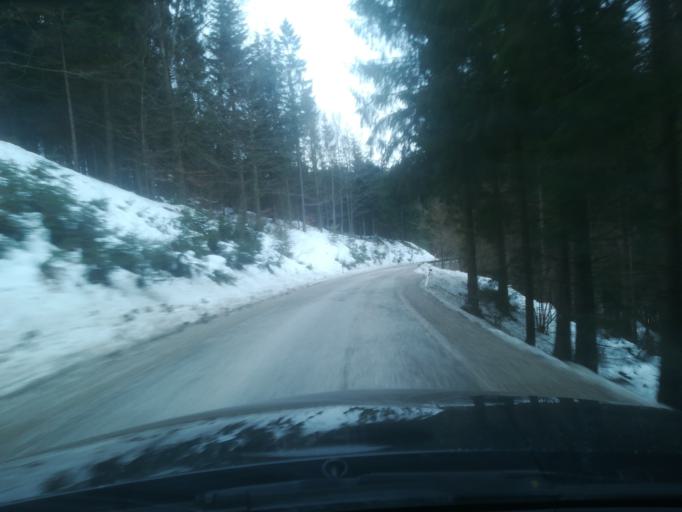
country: AT
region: Upper Austria
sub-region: Politischer Bezirk Perg
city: Perg
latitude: 48.4174
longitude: 14.6536
